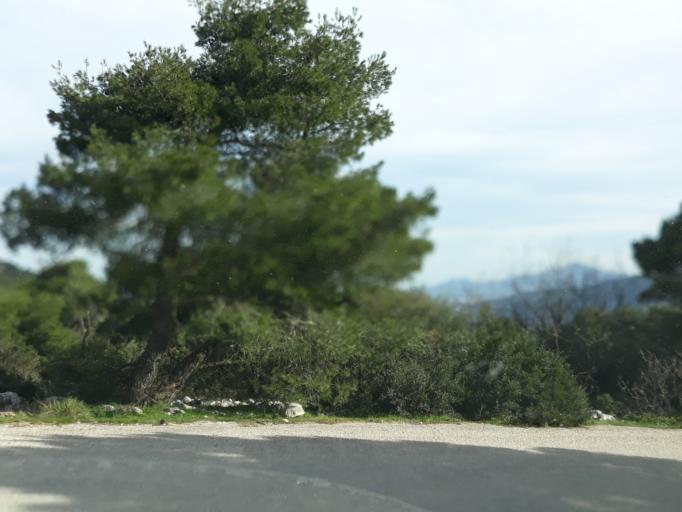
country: GR
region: Attica
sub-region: Nomarchia Anatolikis Attikis
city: Afidnes
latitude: 38.2182
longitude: 23.7957
